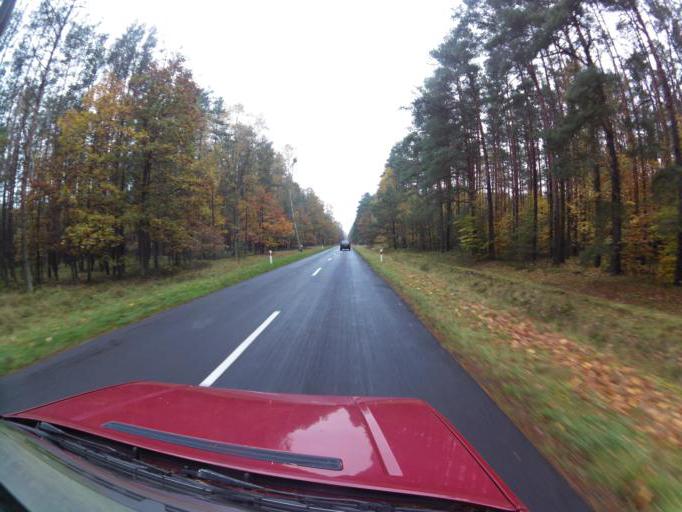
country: PL
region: West Pomeranian Voivodeship
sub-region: Powiat policki
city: Dobra
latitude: 53.5694
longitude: 14.4374
